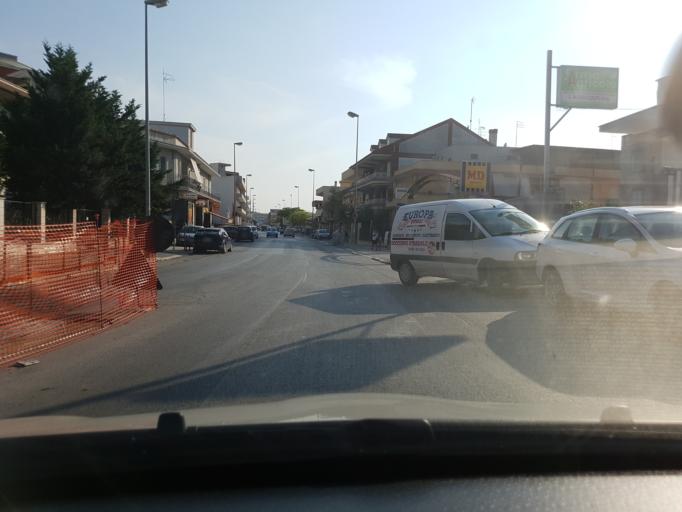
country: IT
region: Apulia
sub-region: Provincia di Foggia
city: Cerignola
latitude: 41.2715
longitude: 15.8945
